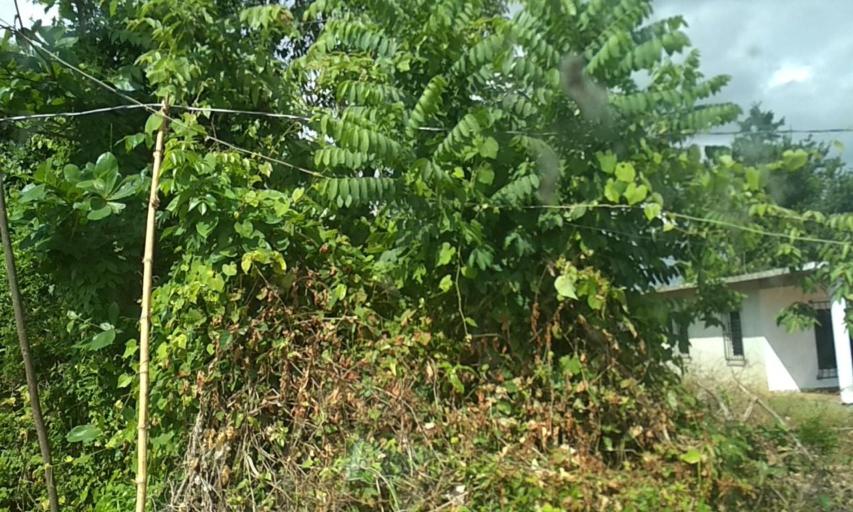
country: MX
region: Puebla
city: San Jose Acateno
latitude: 20.2819
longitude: -97.1306
